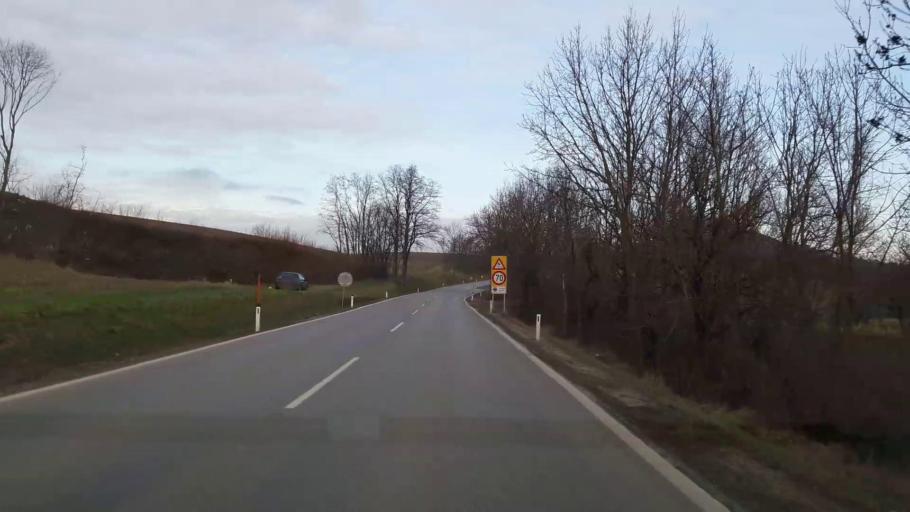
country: AT
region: Lower Austria
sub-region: Politischer Bezirk Mistelbach
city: Staatz
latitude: 48.6670
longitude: 16.4928
